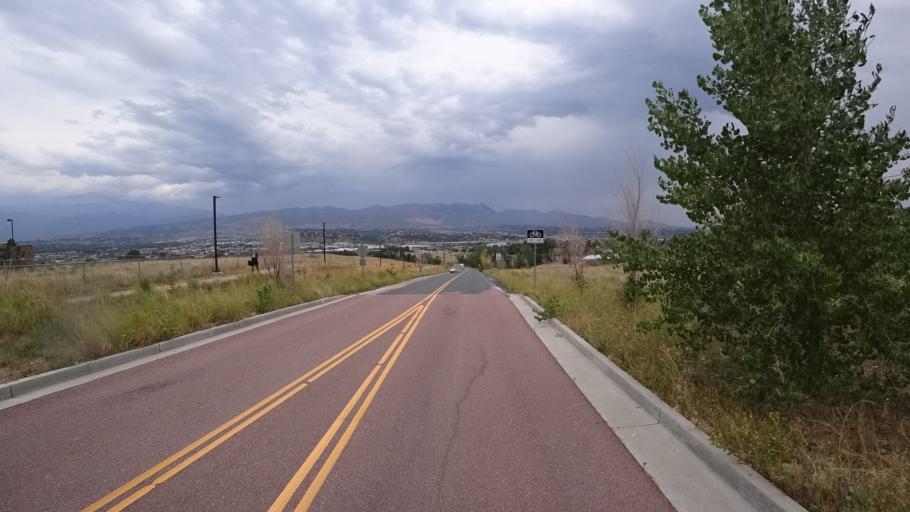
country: US
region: Colorado
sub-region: El Paso County
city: Colorado Springs
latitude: 38.8990
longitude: -104.8065
